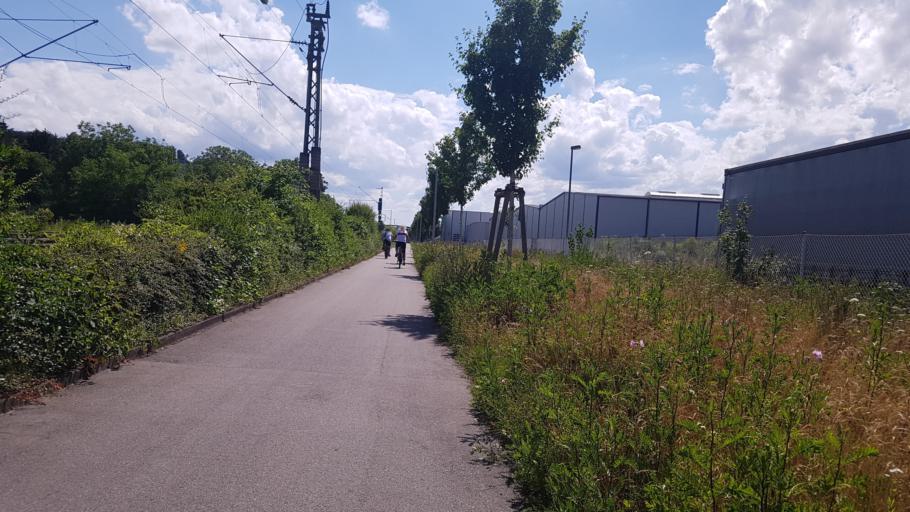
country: DE
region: Baden-Wuerttemberg
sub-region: Karlsruhe Region
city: Bruchsal
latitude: 49.1175
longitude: 8.5829
